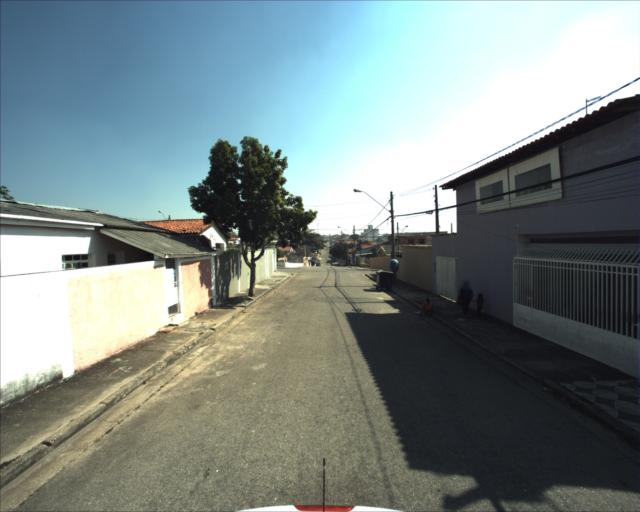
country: BR
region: Sao Paulo
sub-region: Sorocaba
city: Sorocaba
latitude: -23.5019
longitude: -47.4309
